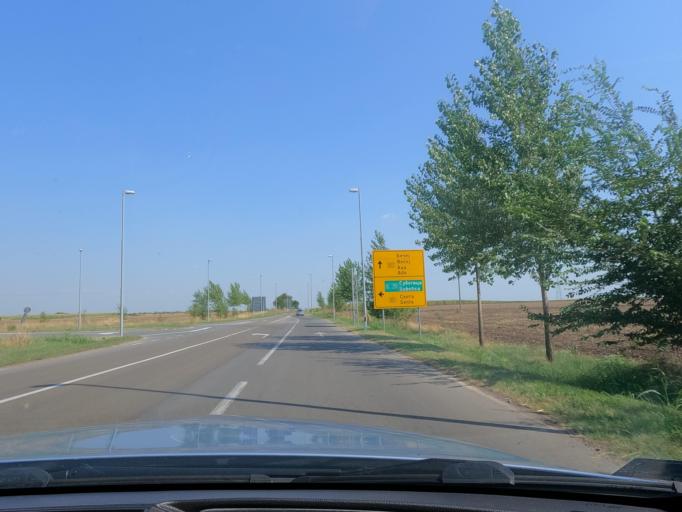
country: RS
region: Autonomna Pokrajina Vojvodina
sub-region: Severnobacki Okrug
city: Backa Topola
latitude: 45.8009
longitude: 19.6581
